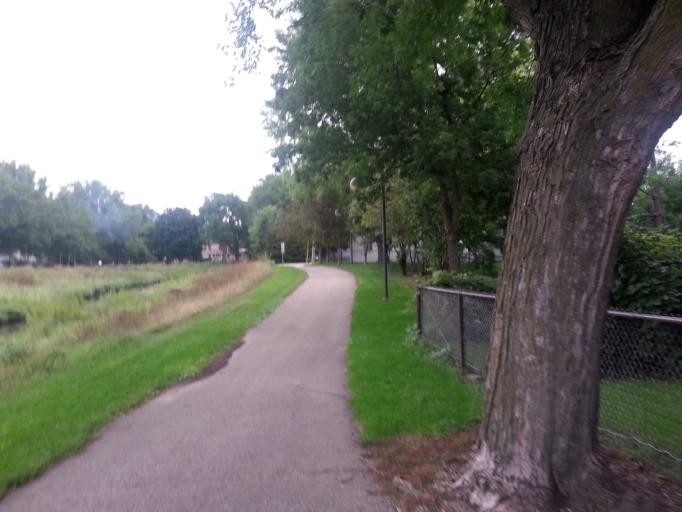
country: US
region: Minnesota
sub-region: Olmsted County
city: Rochester
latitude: 44.0336
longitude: -92.4697
